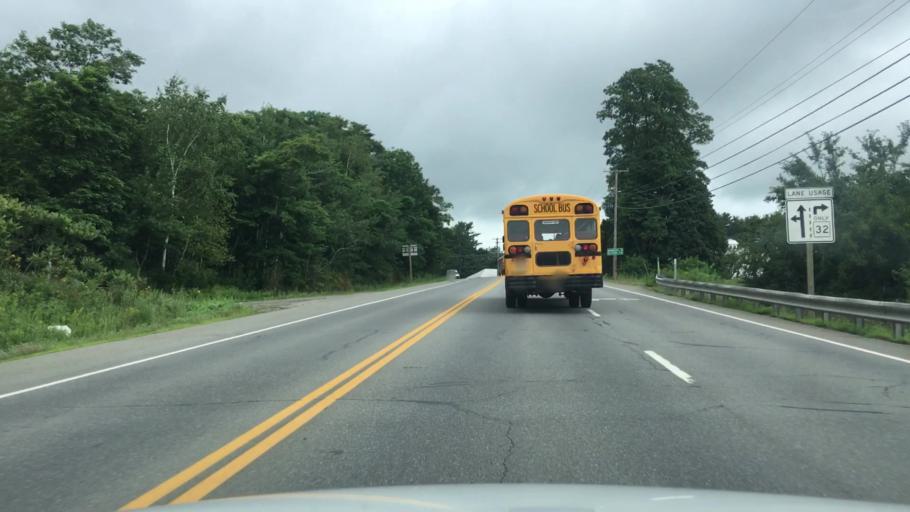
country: US
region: Maine
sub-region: Kennebec County
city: Windsor
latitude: 44.2782
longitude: -69.5965
